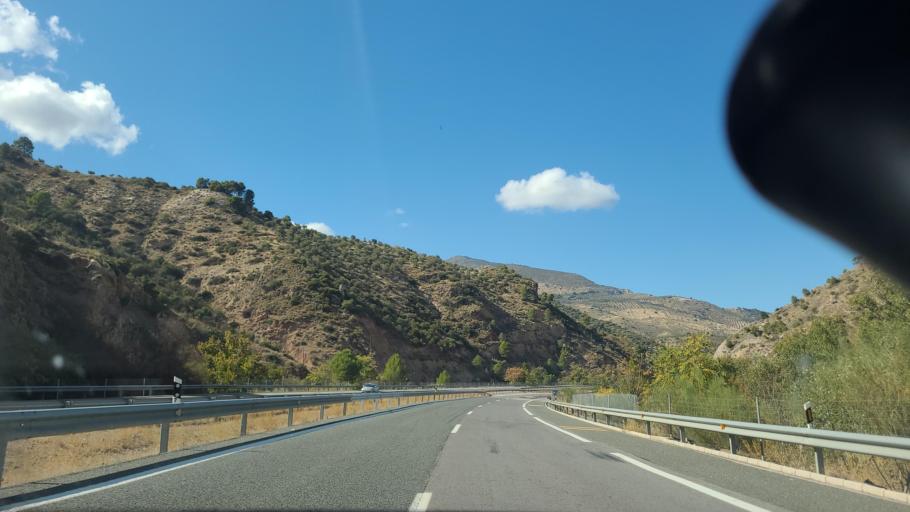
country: ES
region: Andalusia
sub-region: Provincia de Jaen
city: Cambil
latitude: 37.6587
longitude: -3.6098
